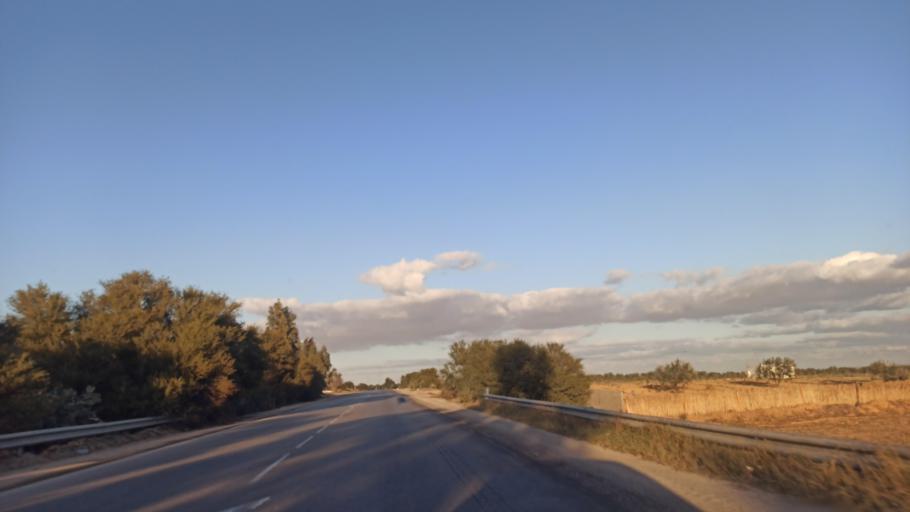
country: TN
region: Al Qayrawan
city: Sbikha
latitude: 35.8728
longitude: 10.2188
